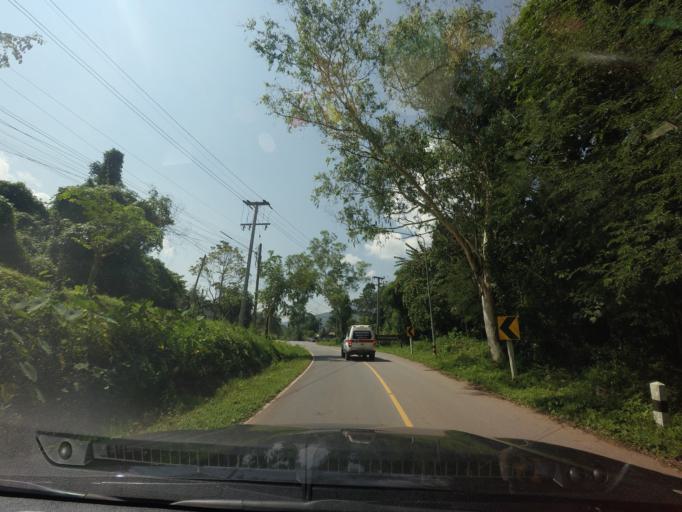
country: TH
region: Nan
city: Bo Kluea
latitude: 19.1459
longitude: 101.1544
